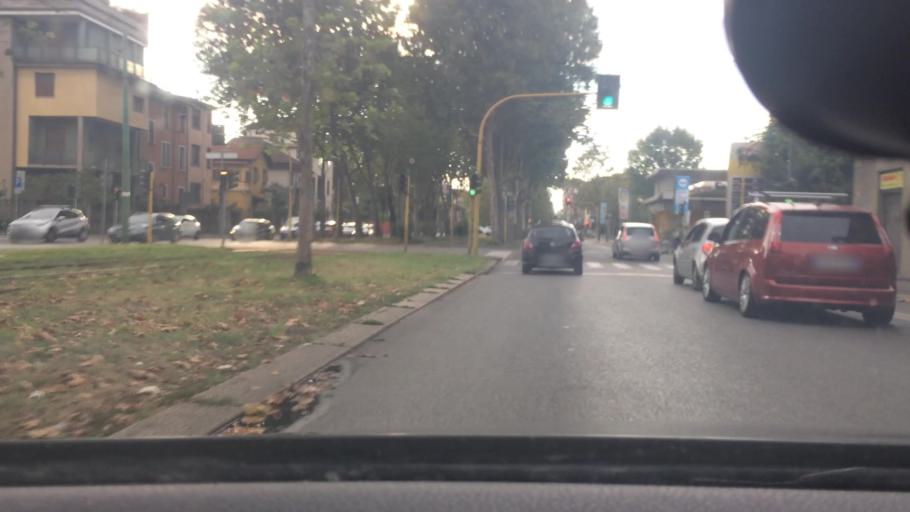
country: IT
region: Lombardy
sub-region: Citta metropolitana di Milano
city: Milano
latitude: 45.4951
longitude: 9.1967
